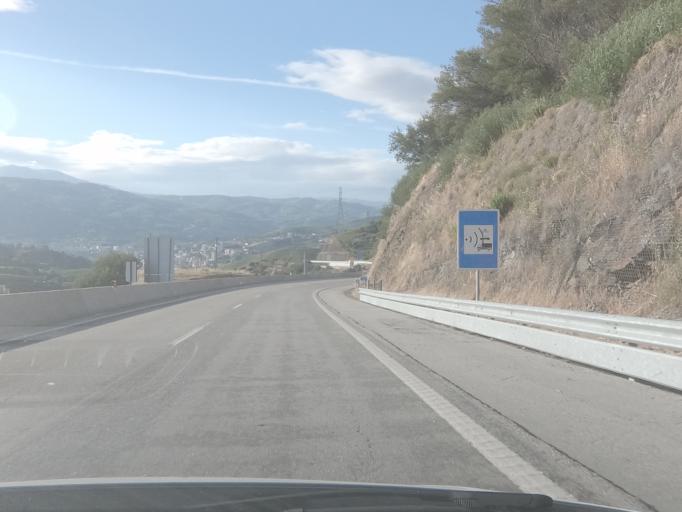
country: PT
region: Vila Real
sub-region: Peso da Regua
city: Peso da Regua
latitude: 41.1374
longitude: -7.7721
